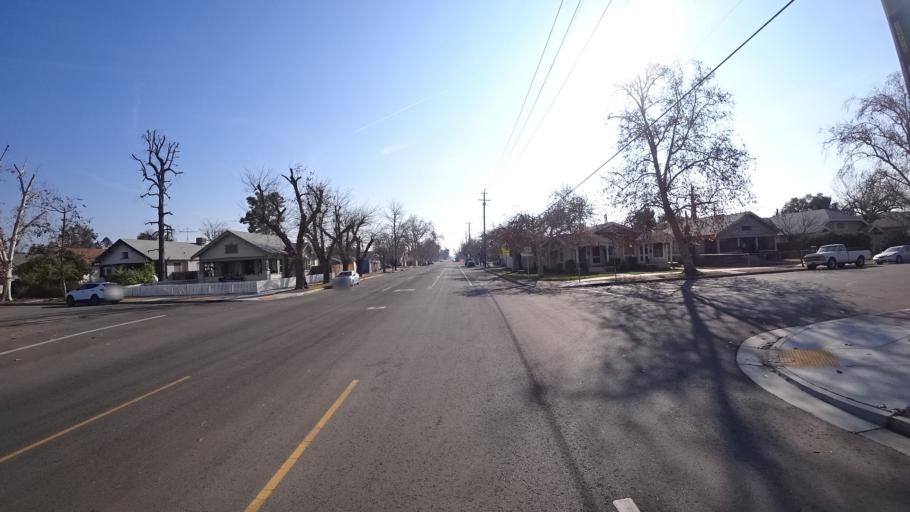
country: US
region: California
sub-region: Kern County
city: Bakersfield
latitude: 35.3668
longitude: -119.0294
